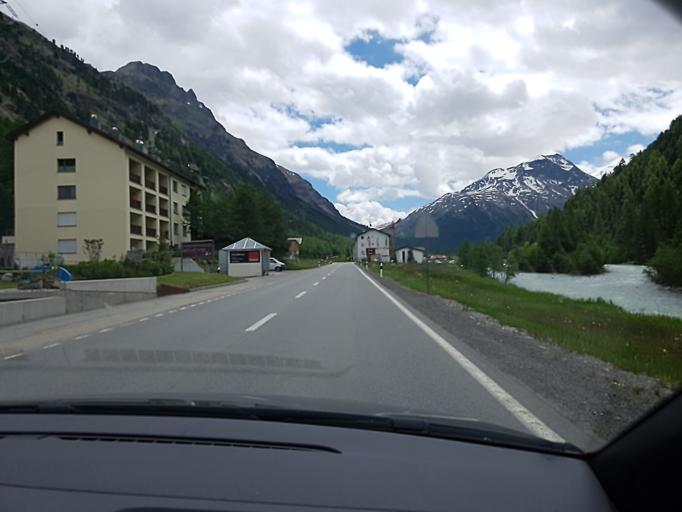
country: CH
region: Grisons
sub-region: Maloja District
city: Pontresina
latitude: 46.4825
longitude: 9.9136
